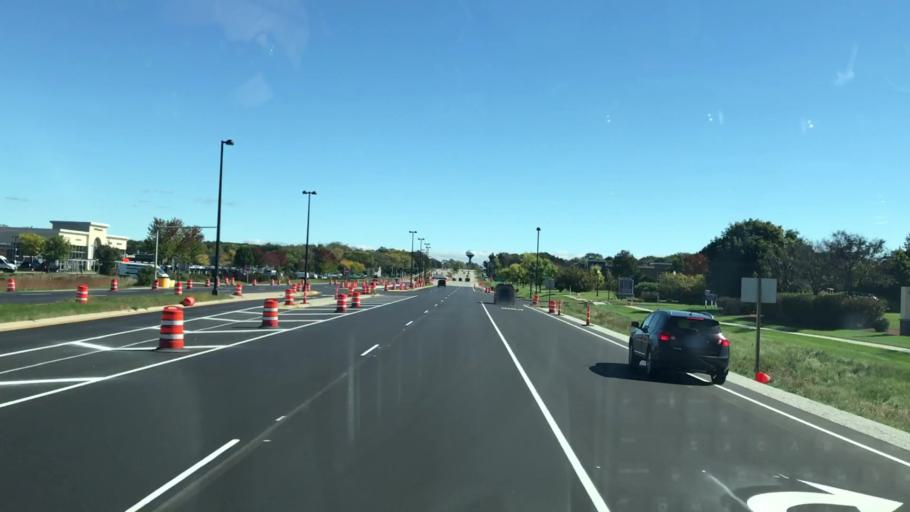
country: US
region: Wisconsin
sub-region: Waukesha County
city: Brookfield
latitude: 43.0904
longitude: -88.1523
